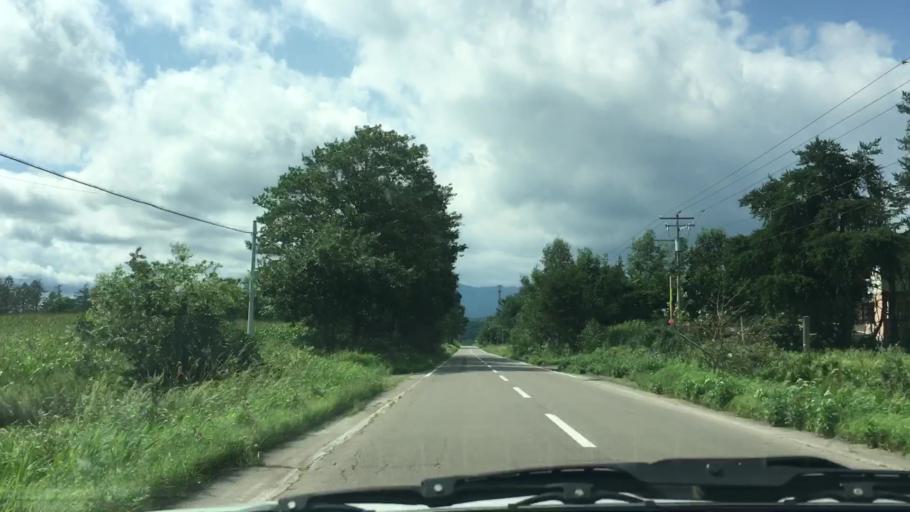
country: JP
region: Hokkaido
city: Otofuke
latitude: 43.2827
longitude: 143.3198
